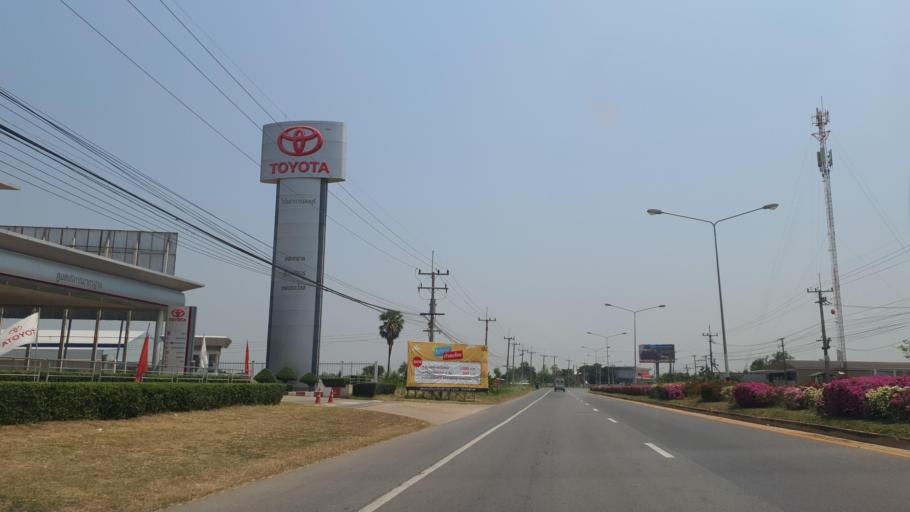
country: TH
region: Kanchanaburi
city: Phanom Thuan
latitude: 14.2415
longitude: 99.8072
